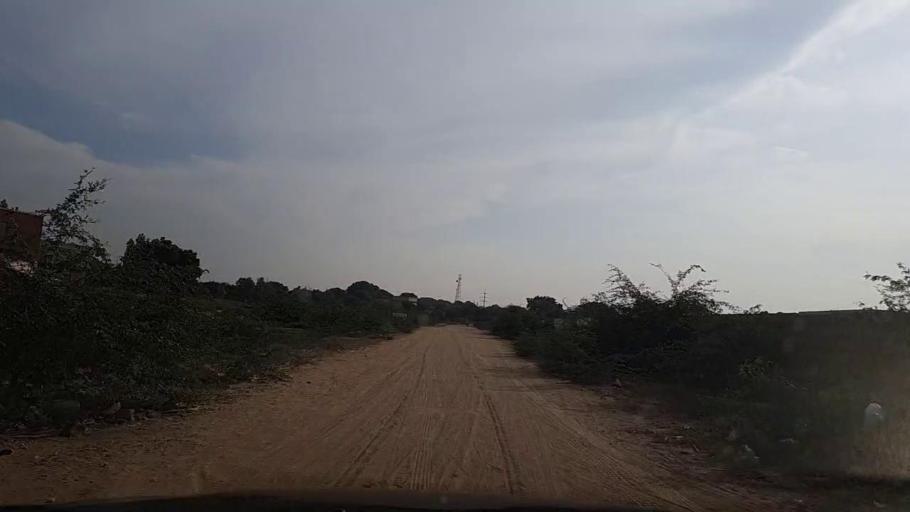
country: PK
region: Sindh
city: Gharo
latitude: 24.7926
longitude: 67.5314
